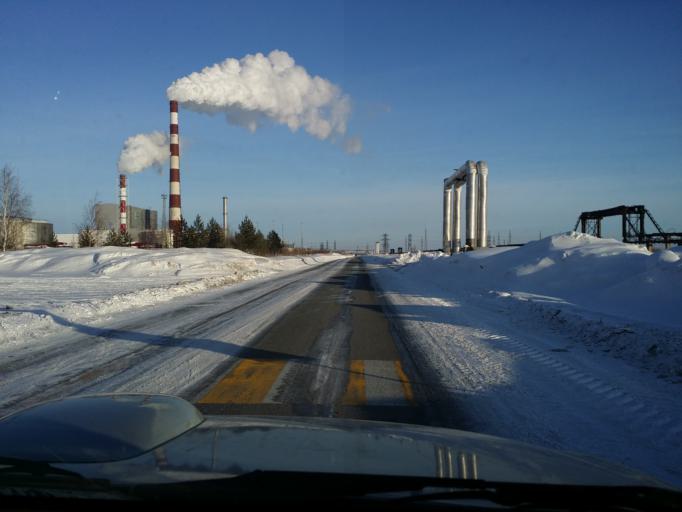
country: RU
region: Khanty-Mansiyskiy Avtonomnyy Okrug
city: Izluchinsk
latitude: 60.9783
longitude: 76.9223
